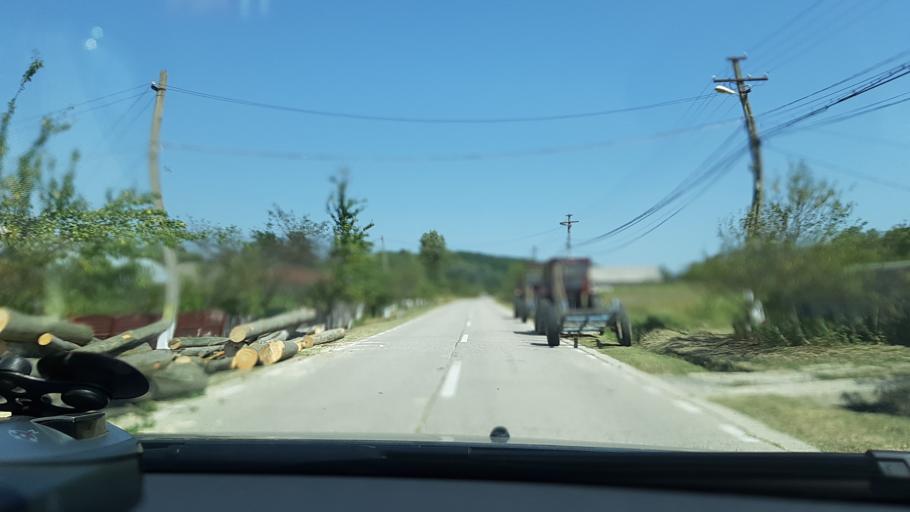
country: RO
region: Gorj
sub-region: Comuna Logresti-Mosteni
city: Logresti Mosteni
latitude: 44.8969
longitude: 23.7311
